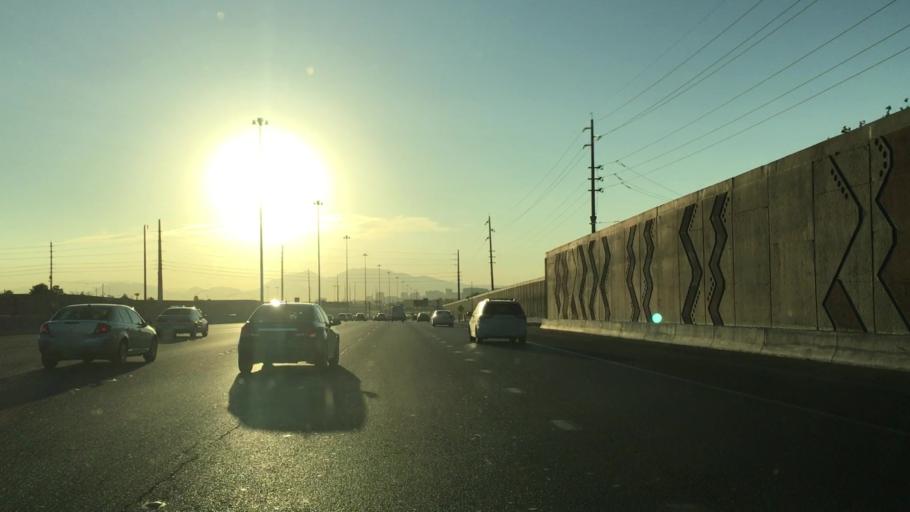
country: US
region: Nevada
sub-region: Clark County
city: Spring Valley
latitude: 36.1733
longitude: -115.2181
